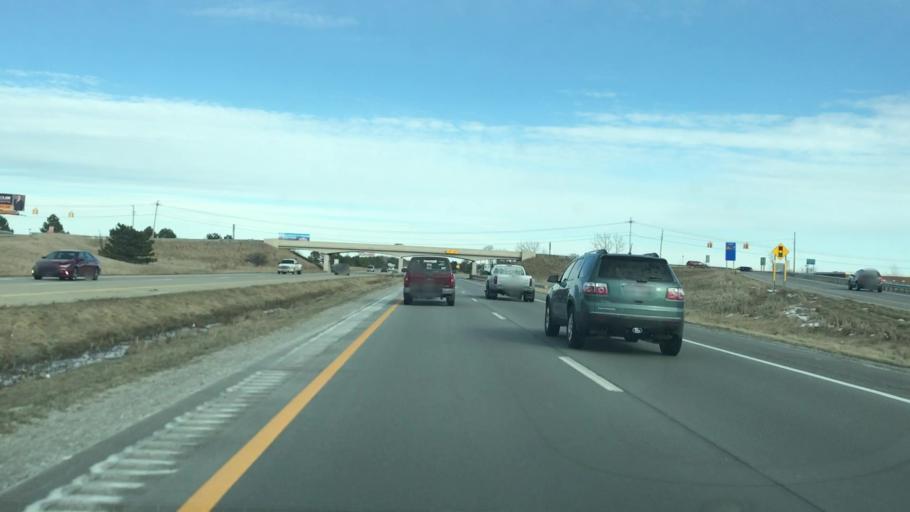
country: US
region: Michigan
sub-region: Bay County
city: Auburn
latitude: 43.5960
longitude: -83.9948
